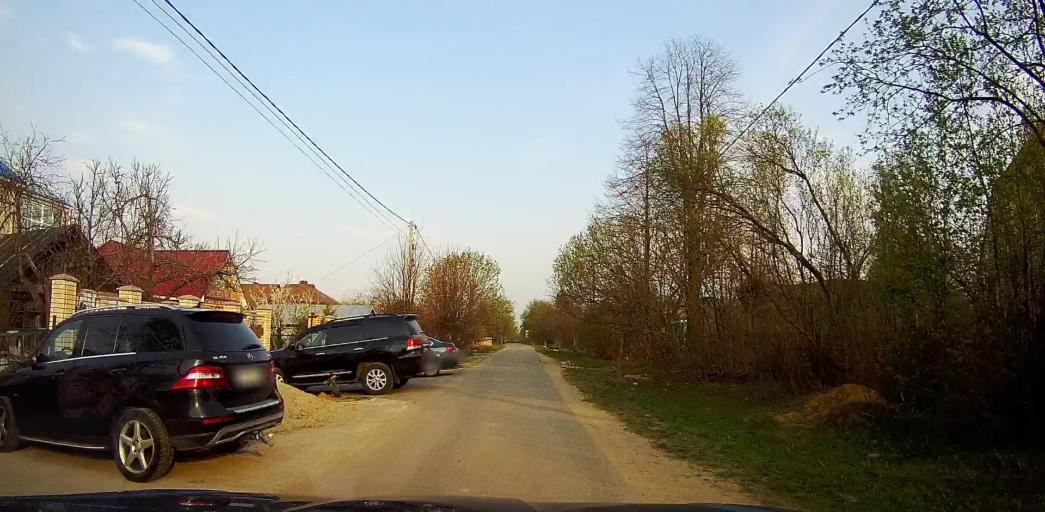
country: RU
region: Moskovskaya
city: Andreyevskoye
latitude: 55.5503
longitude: 37.9524
